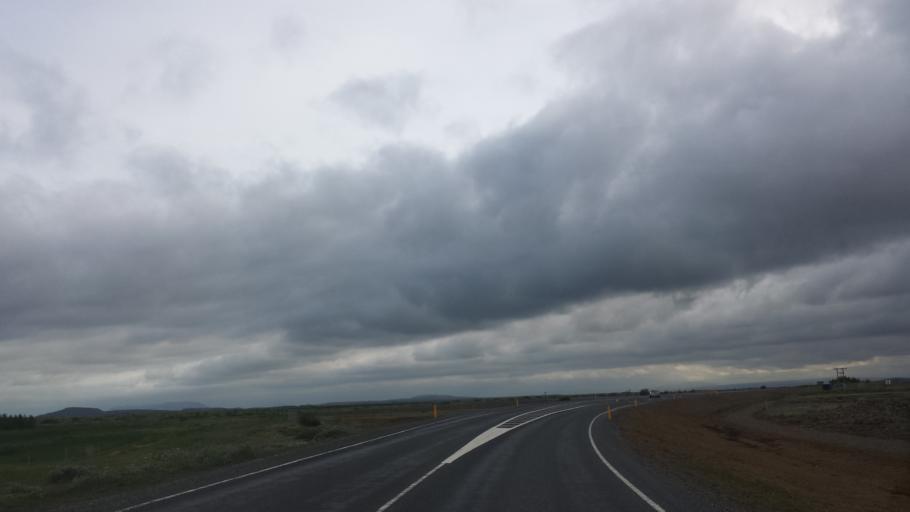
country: IS
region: South
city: Selfoss
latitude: 64.2743
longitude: -20.3544
